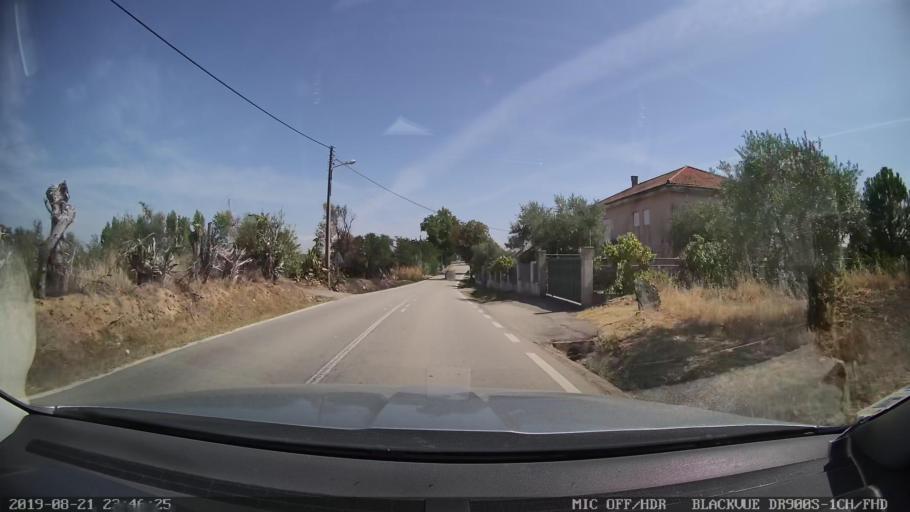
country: PT
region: Castelo Branco
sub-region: Idanha-A-Nova
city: Idanha-a-Nova
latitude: 39.8412
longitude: -7.2586
